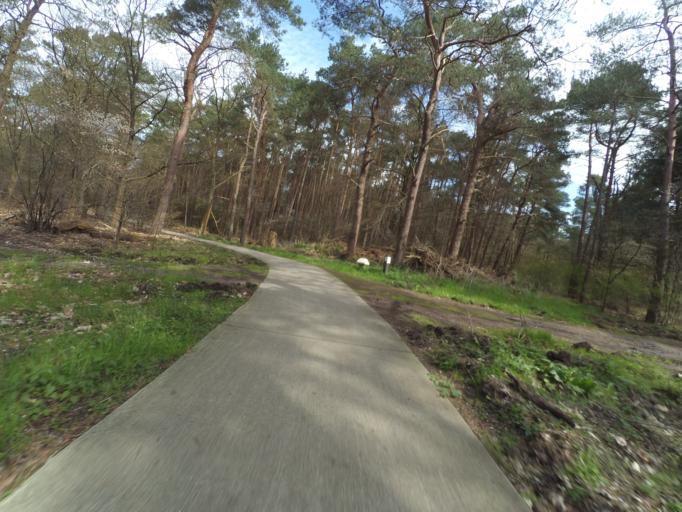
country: NL
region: Gelderland
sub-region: Gemeente Nunspeet
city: Nunspeet
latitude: 52.3428
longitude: 5.8093
